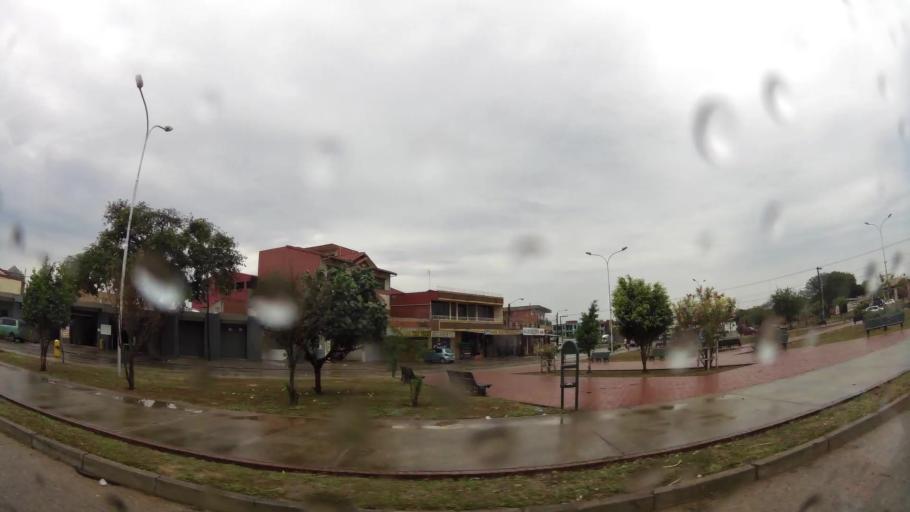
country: BO
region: Santa Cruz
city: Santa Cruz de la Sierra
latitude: -17.8173
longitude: -63.2000
